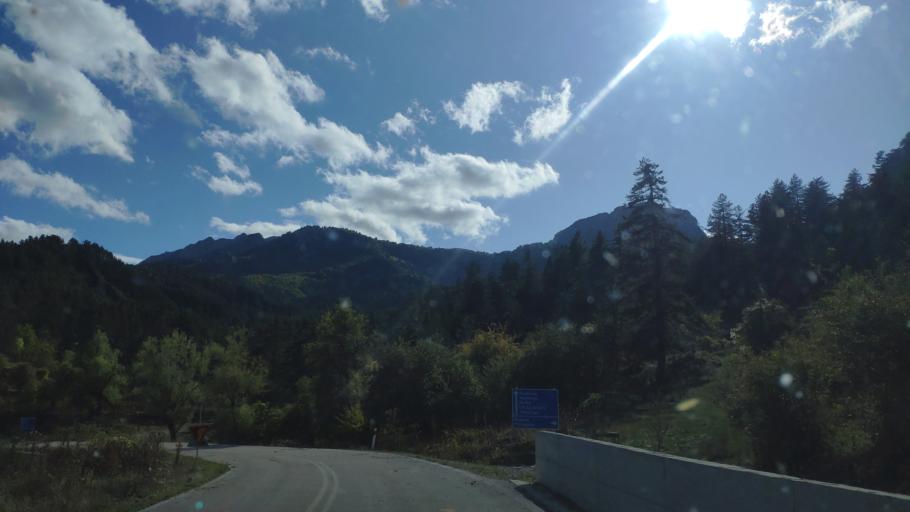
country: AL
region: Korce
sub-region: Rrethi i Devollit
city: Miras
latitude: 40.3988
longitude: 20.8822
